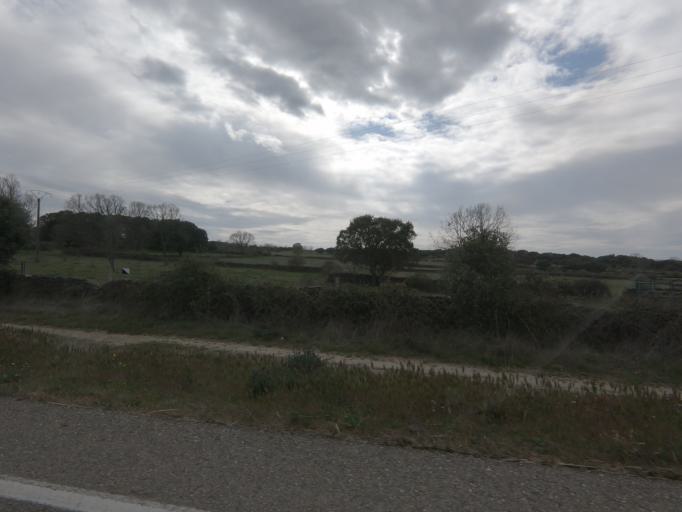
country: ES
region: Castille and Leon
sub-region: Provincia de Salamanca
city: Robleda
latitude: 40.3941
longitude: -6.6067
